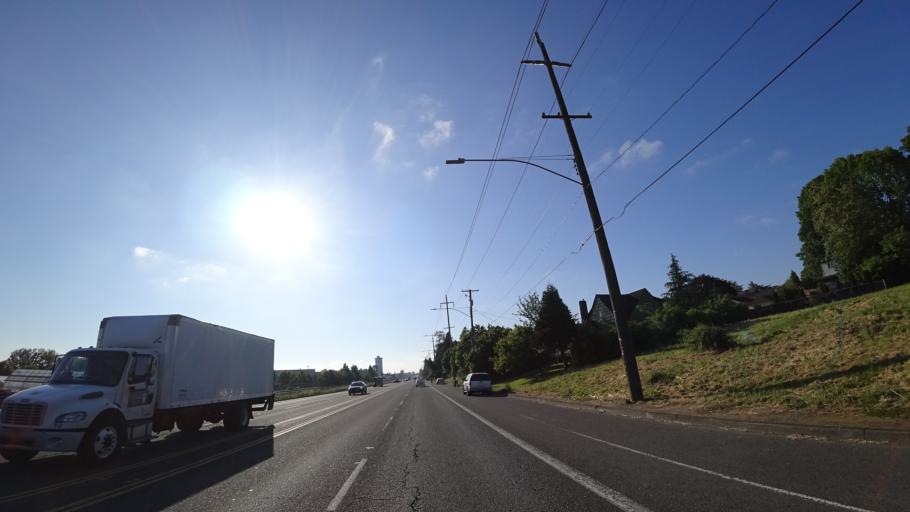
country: US
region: Oregon
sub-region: Multnomah County
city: Portland
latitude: 45.5758
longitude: -122.6476
